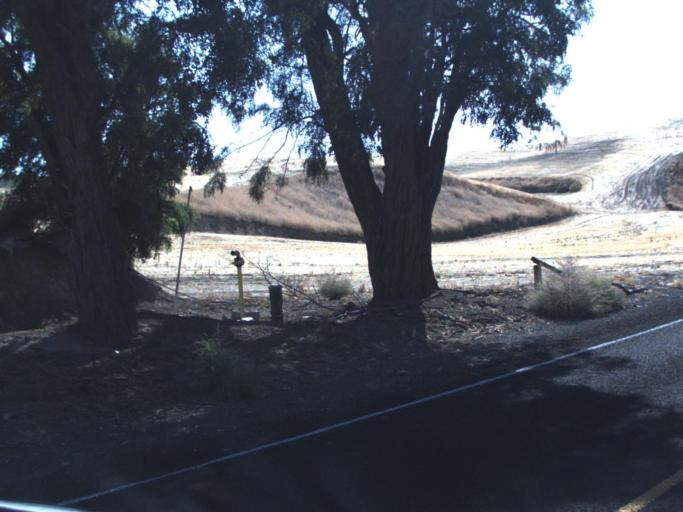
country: US
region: Washington
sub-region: Walla Walla County
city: Walla Walla
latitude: 46.2345
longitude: -118.3727
